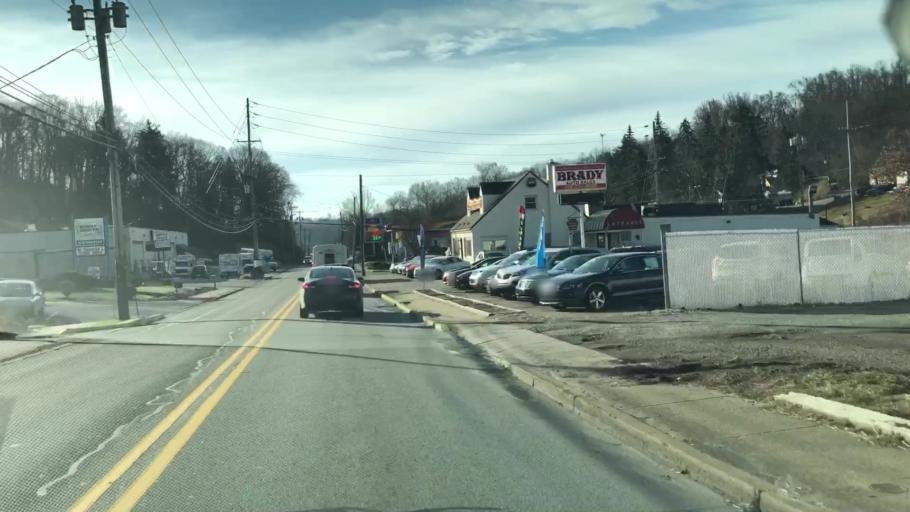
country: US
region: Pennsylvania
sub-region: Allegheny County
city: Churchill
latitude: 40.4505
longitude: -79.8269
